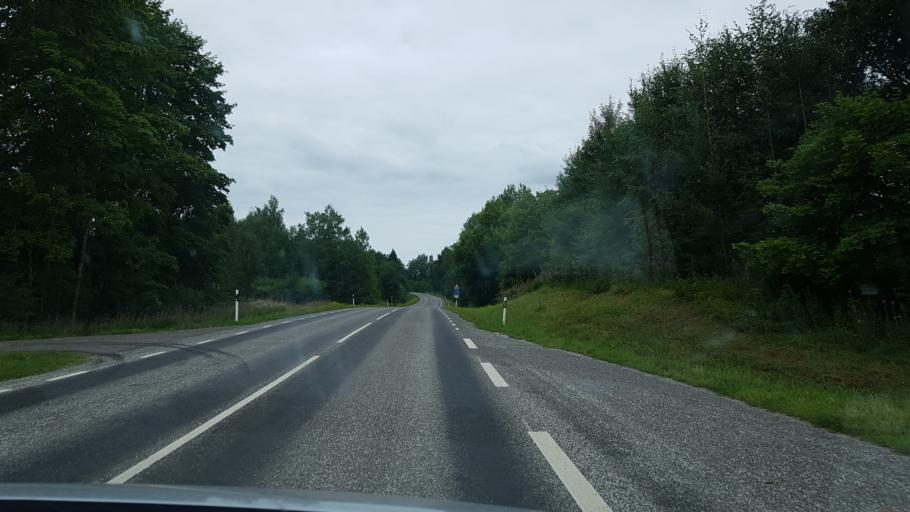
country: EE
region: Vorumaa
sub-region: Antsla vald
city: Vana-Antsla
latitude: 58.0115
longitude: 26.5972
